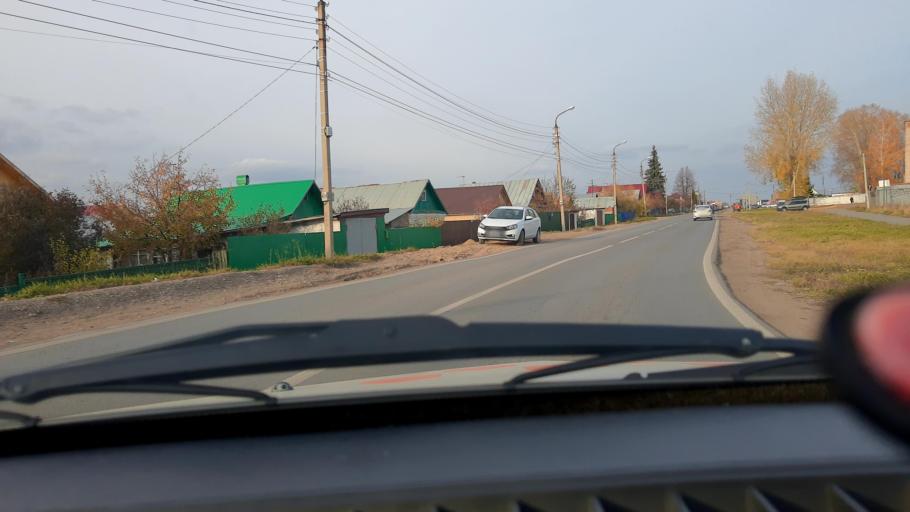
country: RU
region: Bashkortostan
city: Iglino
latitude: 54.7880
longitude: 56.2327
